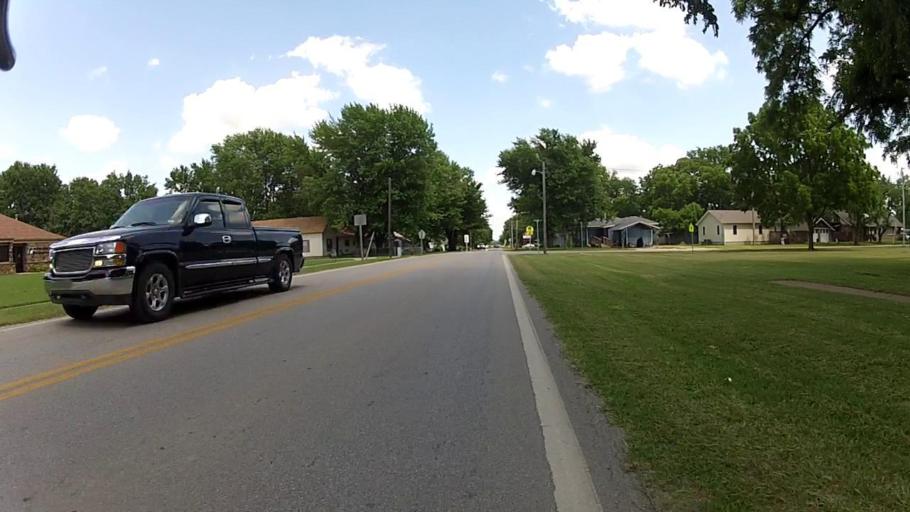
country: US
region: Kansas
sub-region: Labette County
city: Altamont
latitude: 37.1929
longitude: -95.2922
